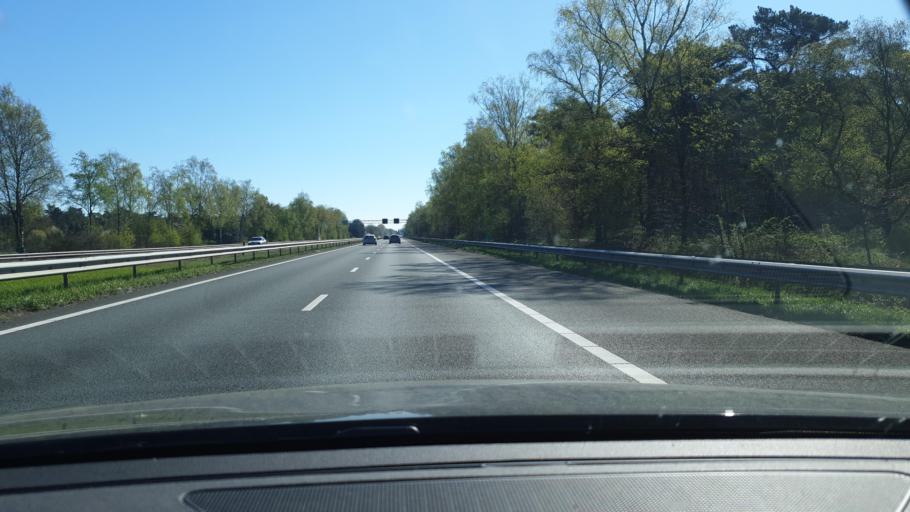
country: NL
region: North Brabant
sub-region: Gemeente Geldrop-Mierlo
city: Mierlo
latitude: 51.4246
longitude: 5.6542
